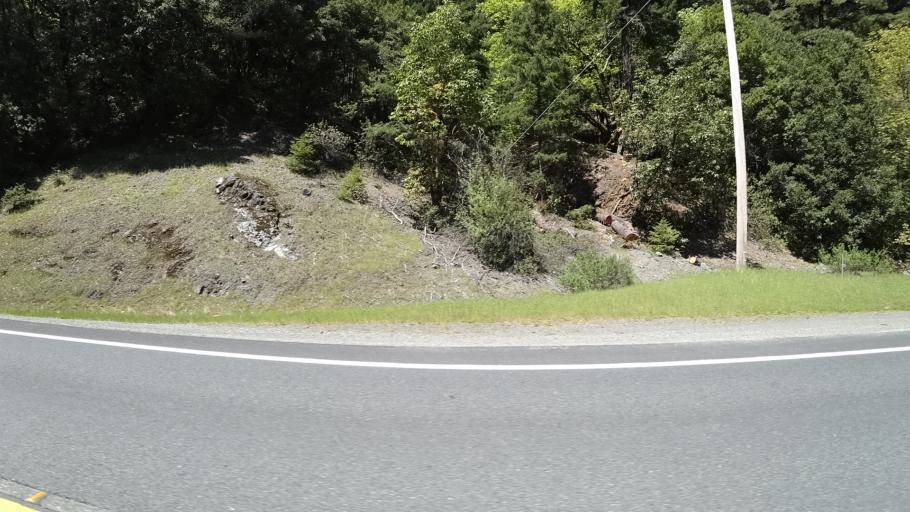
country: US
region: California
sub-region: Humboldt County
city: Willow Creek
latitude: 40.9244
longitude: -123.6916
